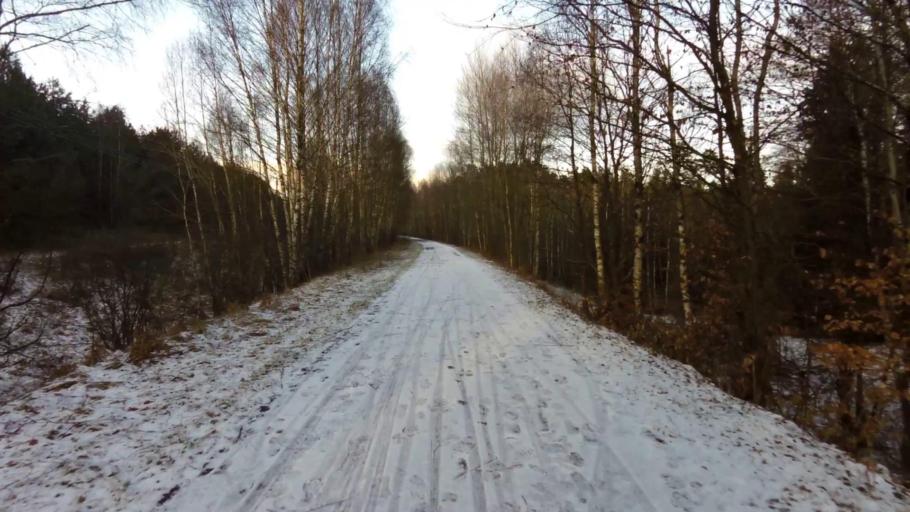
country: PL
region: West Pomeranian Voivodeship
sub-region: Powiat drawski
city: Zlocieniec
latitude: 53.5627
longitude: 16.0347
